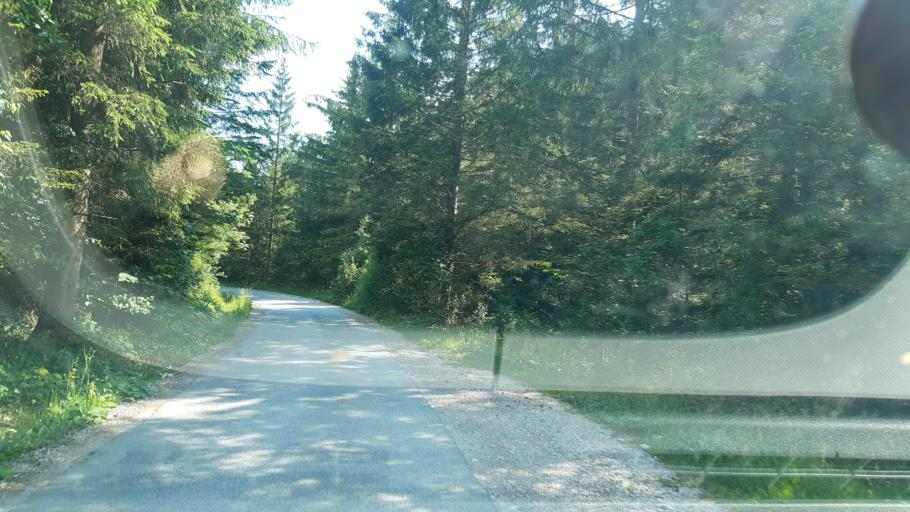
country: SI
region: Radovljica
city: Radovljica
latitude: 46.3897
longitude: 14.2174
